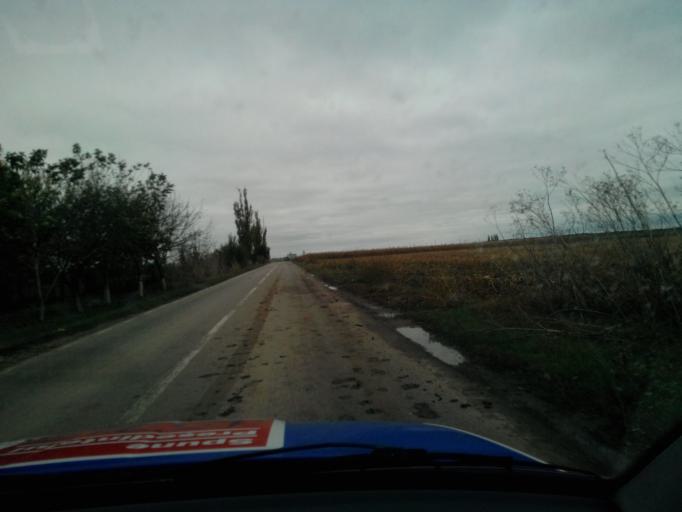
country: RO
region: Giurgiu
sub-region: Comuna Baneasa
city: Pietrele
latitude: 44.0658
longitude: 26.1070
